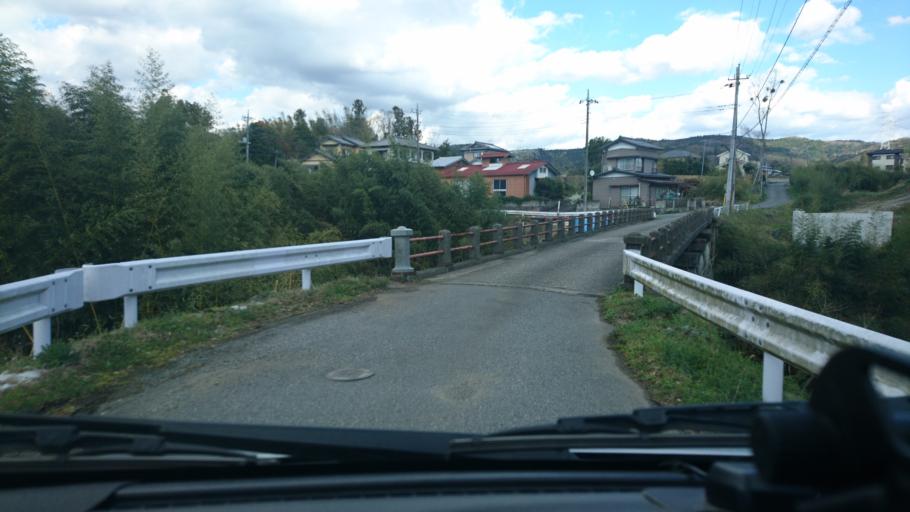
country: JP
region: Chiba
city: Kimitsu
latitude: 35.2873
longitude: 139.9833
